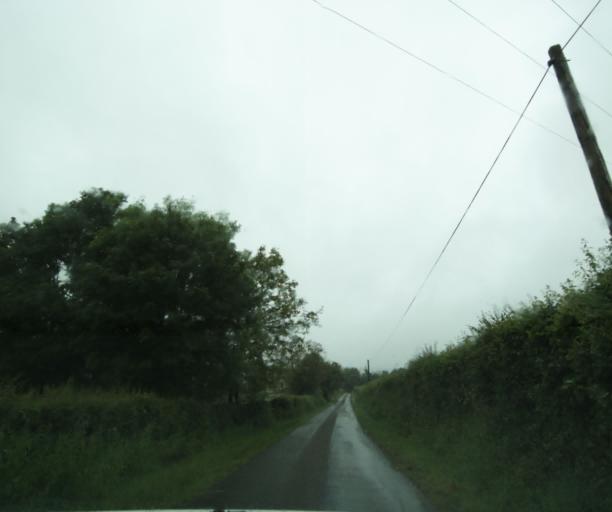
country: FR
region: Bourgogne
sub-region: Departement de Saone-et-Loire
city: Charolles
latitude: 46.4006
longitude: 4.2472
